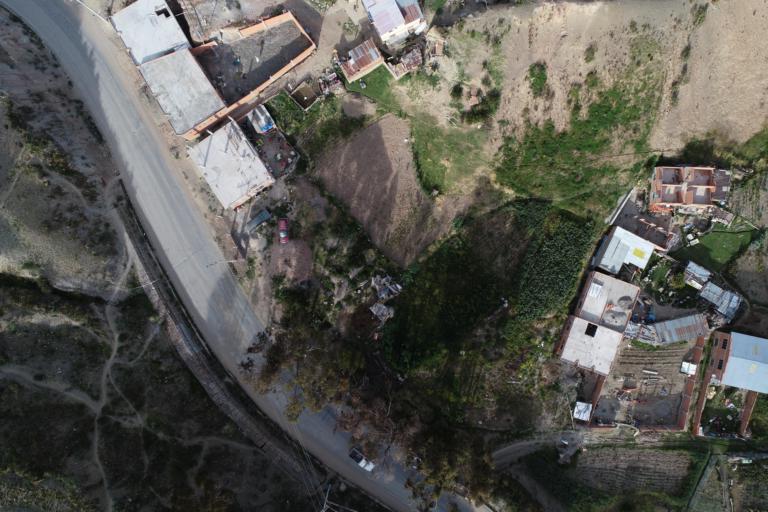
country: BO
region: La Paz
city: La Paz
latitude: -16.5434
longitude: -68.0035
